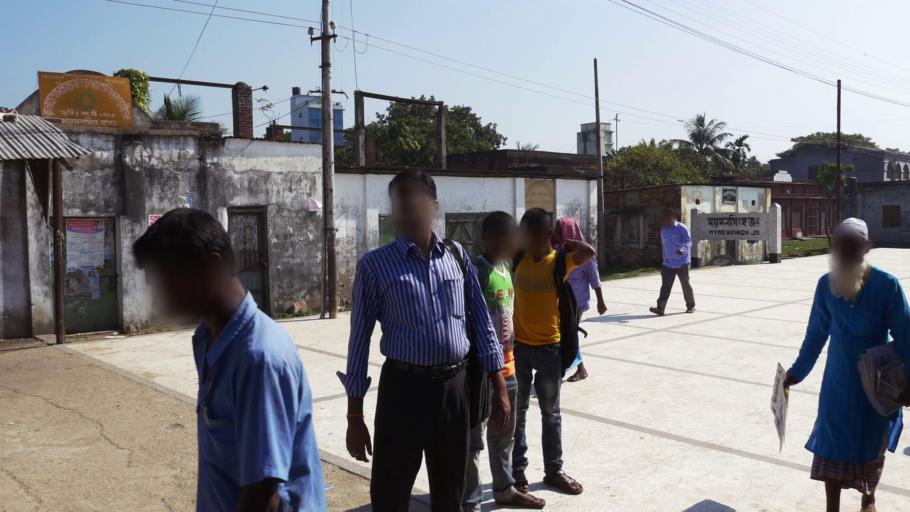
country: BD
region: Dhaka
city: Mymensingh
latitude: 24.6333
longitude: 90.4613
